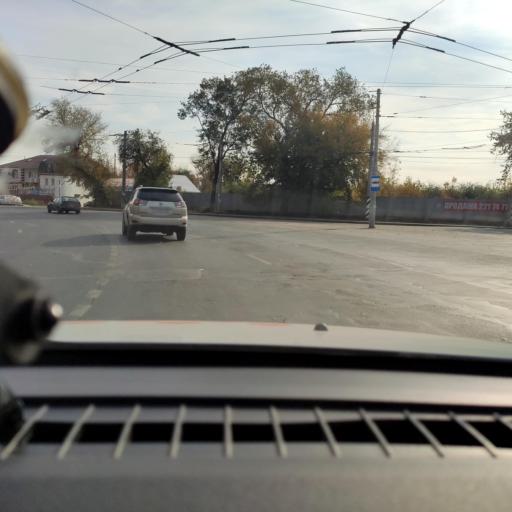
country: RU
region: Samara
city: Rozhdestveno
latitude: 53.1659
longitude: 50.0737
